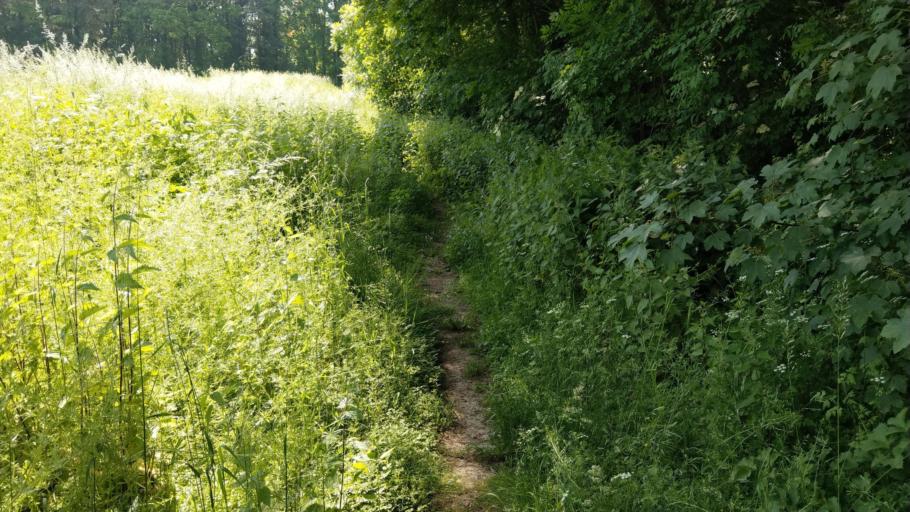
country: NL
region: Limburg
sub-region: Gemeente Vaals
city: Vaals
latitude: 50.7781
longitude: 6.0215
